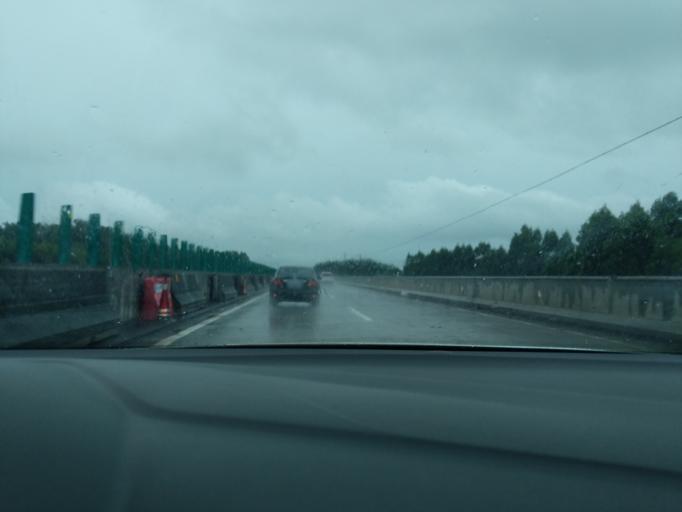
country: CN
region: Guangdong
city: Yueshan
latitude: 22.4630
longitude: 112.7333
